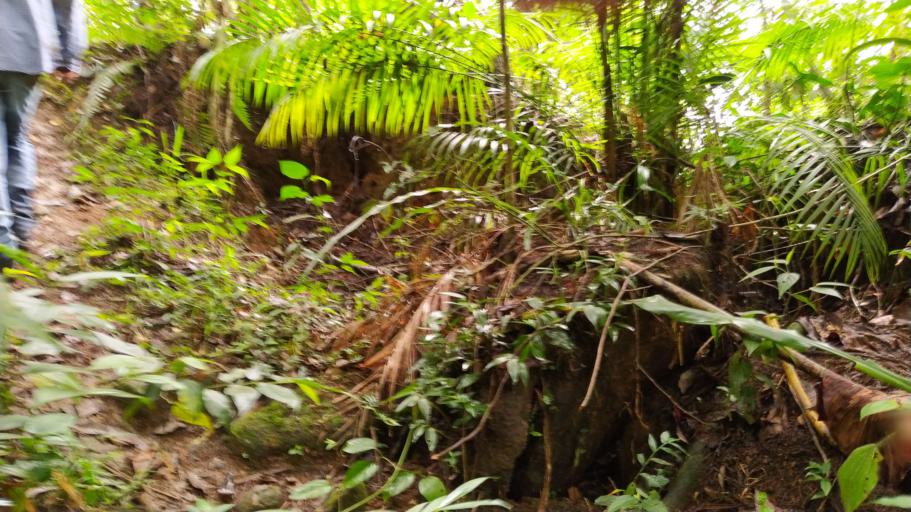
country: CO
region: Valle del Cauca
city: Jamundi
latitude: 3.3182
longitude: -76.5862
